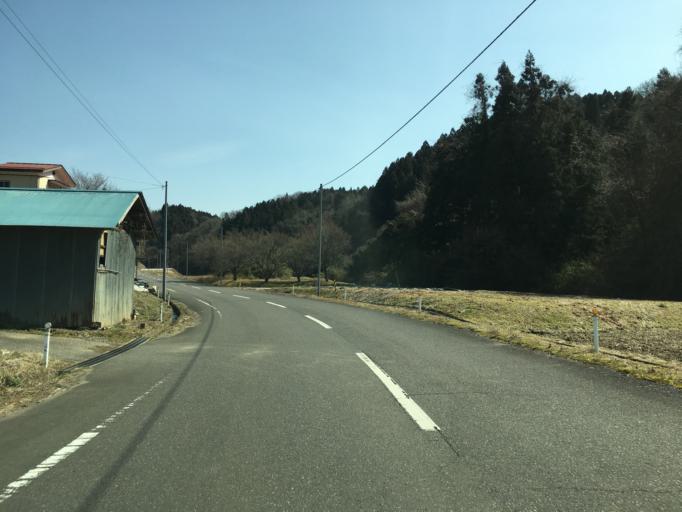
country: JP
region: Fukushima
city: Ishikawa
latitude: 37.1058
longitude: 140.4263
